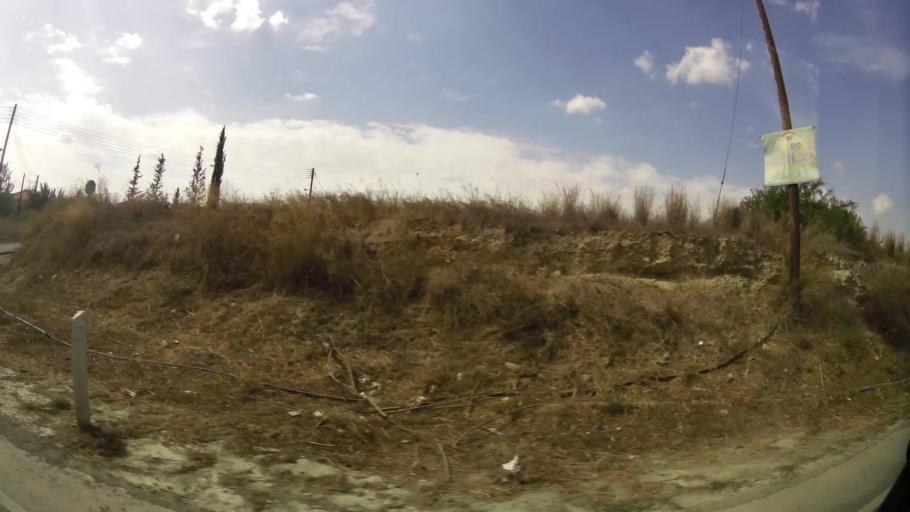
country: CY
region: Lefkosia
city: Tseri
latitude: 35.0912
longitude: 33.3273
